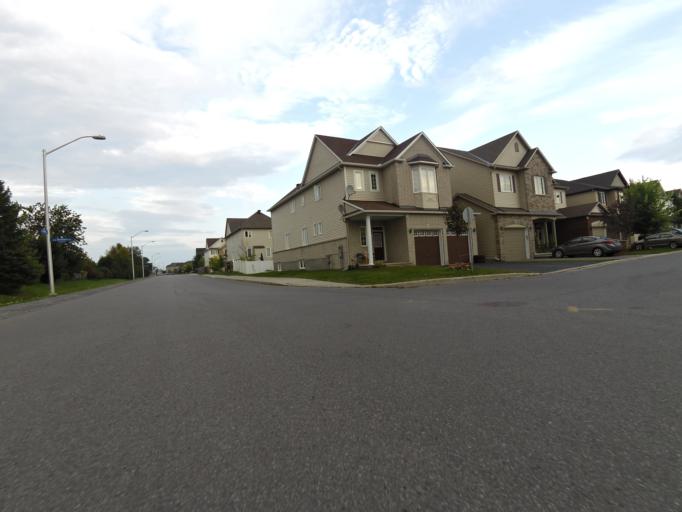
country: CA
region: Ontario
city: Bells Corners
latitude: 45.2630
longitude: -75.7628
